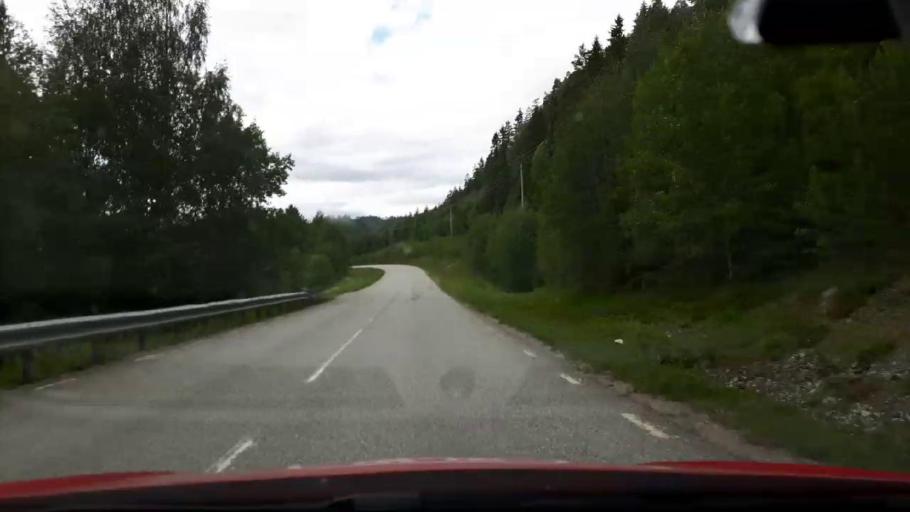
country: SE
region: Jaemtland
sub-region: Ragunda Kommun
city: Hammarstrand
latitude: 62.9652
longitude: 15.9958
